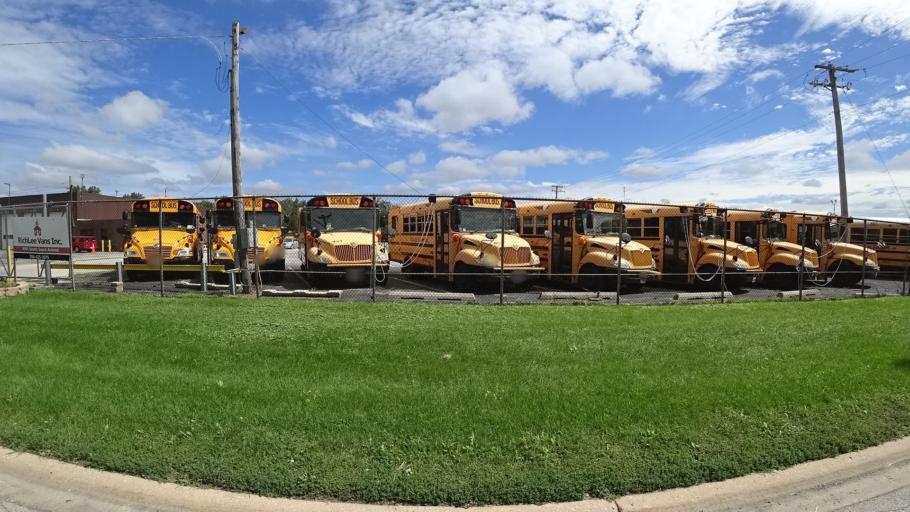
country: US
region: Illinois
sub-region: Cook County
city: Chicago Ridge
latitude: 41.7118
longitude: -87.7938
